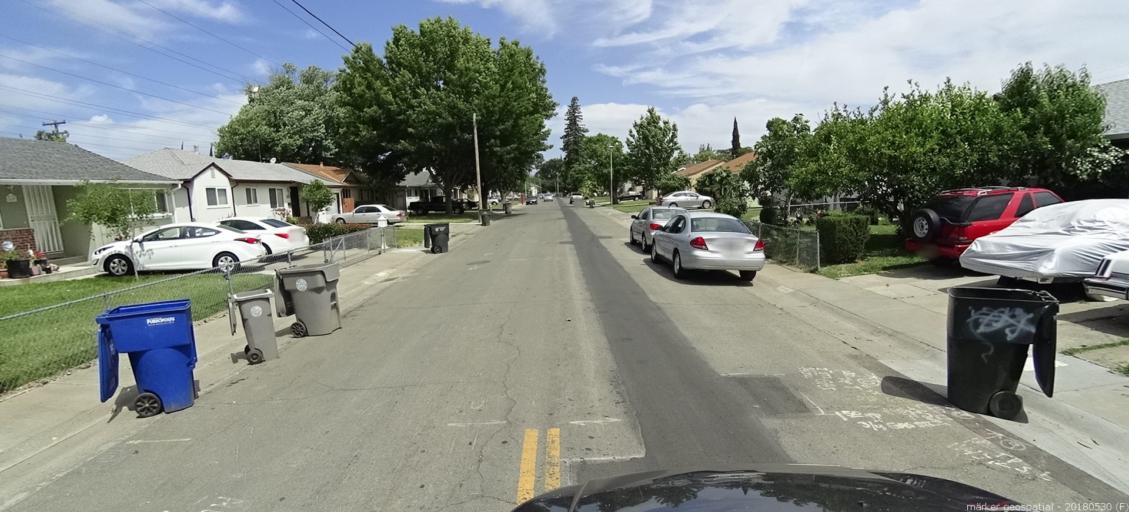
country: US
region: California
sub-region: Sacramento County
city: Sacramento
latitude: 38.6137
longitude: -121.4827
